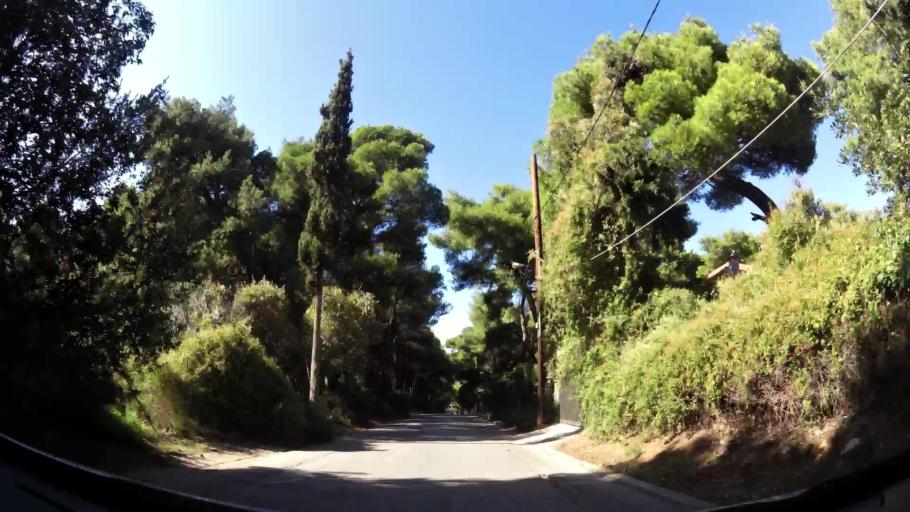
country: GR
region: Attica
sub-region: Nomarchia Athinas
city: Ekali
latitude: 38.1132
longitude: 23.8324
